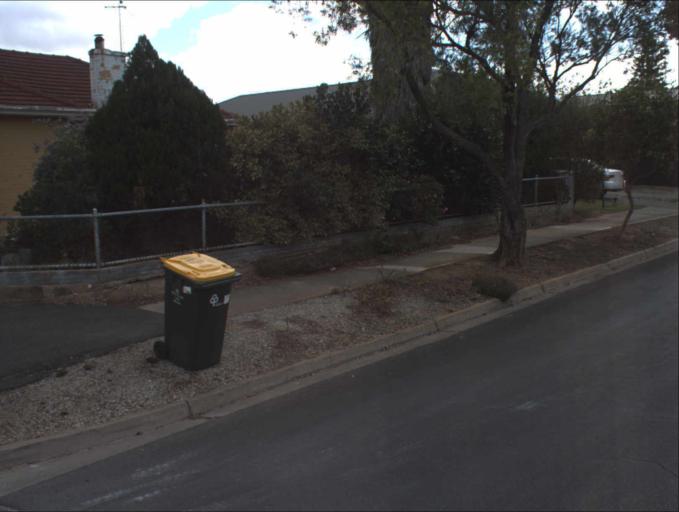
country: AU
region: South Australia
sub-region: Prospect
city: Prospect
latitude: -34.8710
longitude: 138.5877
